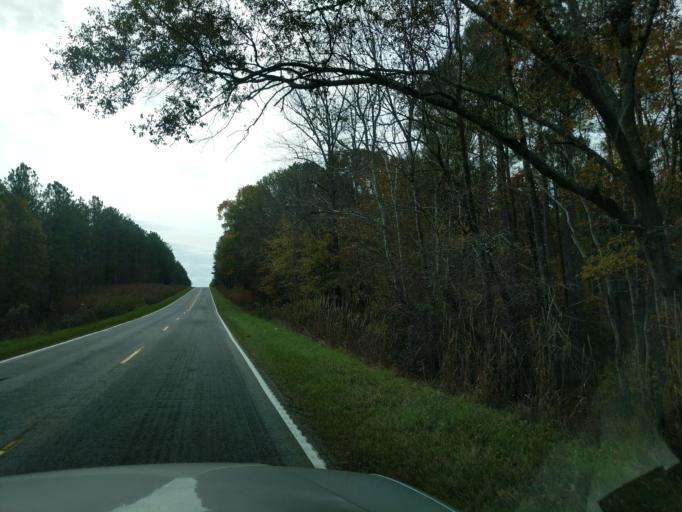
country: US
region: South Carolina
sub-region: Laurens County
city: Joanna
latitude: 34.3071
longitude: -81.8434
